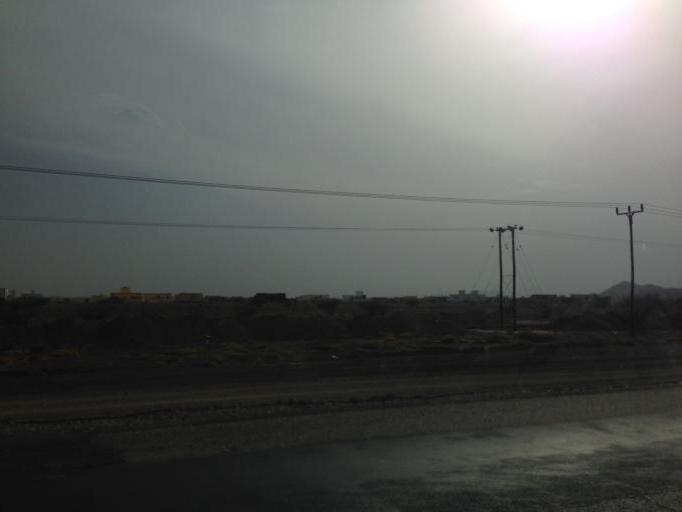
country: OM
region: Ash Sharqiyah
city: Al Qabil
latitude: 22.6279
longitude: 58.6511
